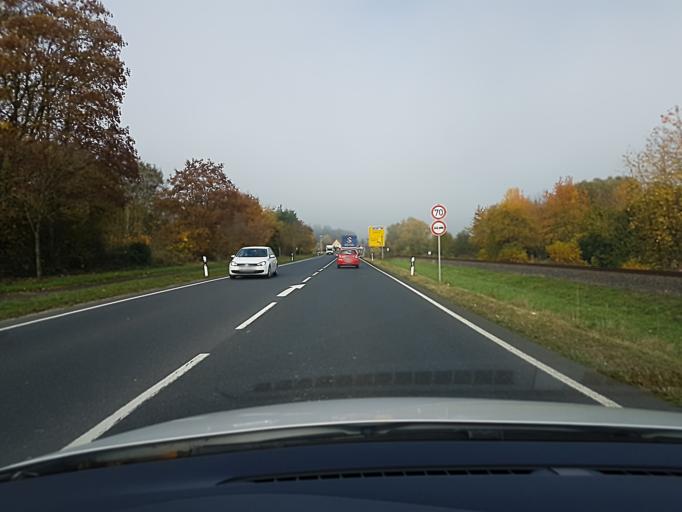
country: DE
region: Bavaria
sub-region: Regierungsbezirk Unterfranken
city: Laudenbach
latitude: 49.7362
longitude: 9.1850
